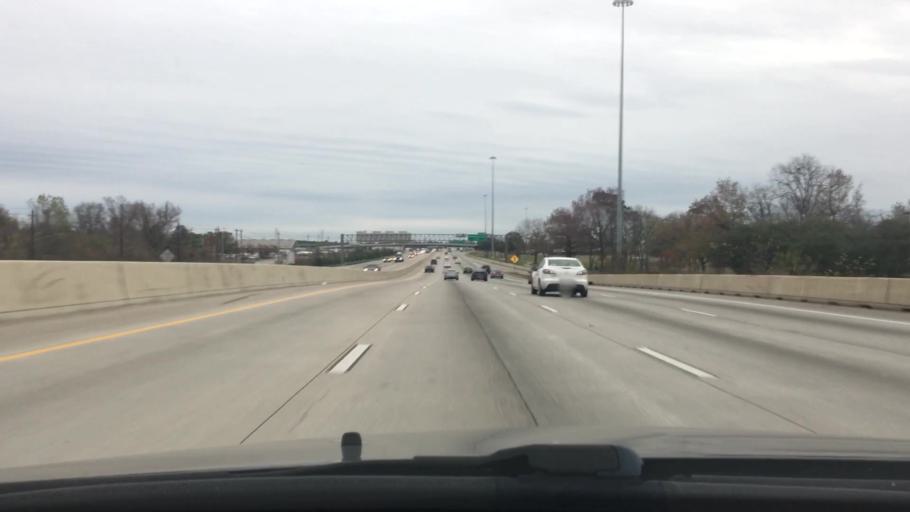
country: US
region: Texas
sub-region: Harris County
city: Houston
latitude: 29.8094
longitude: -95.3159
